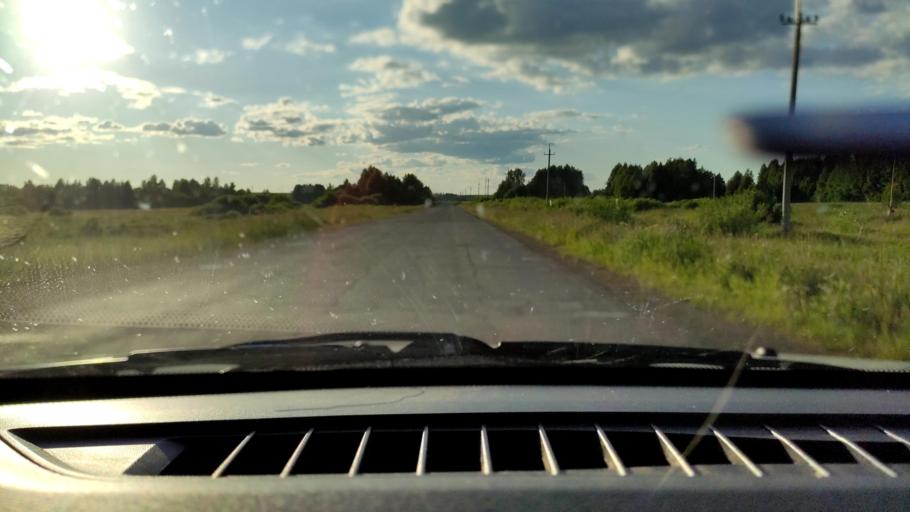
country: RU
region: Perm
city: Uinskoye
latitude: 57.0939
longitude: 56.5511
